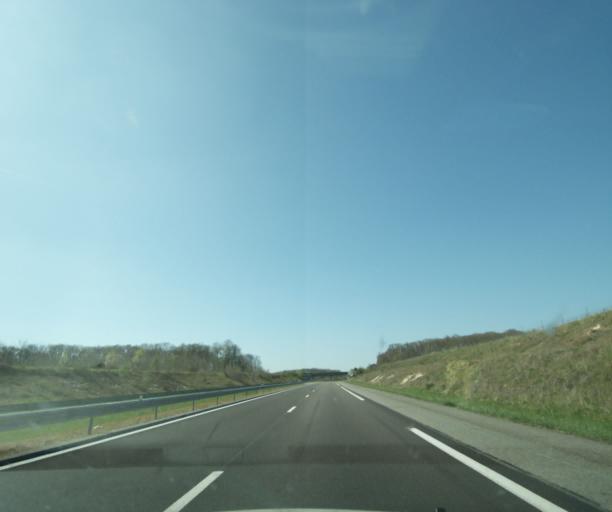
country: FR
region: Centre
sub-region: Departement du Loiret
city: Bonny-sur-Loire
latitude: 47.6107
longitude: 2.8236
